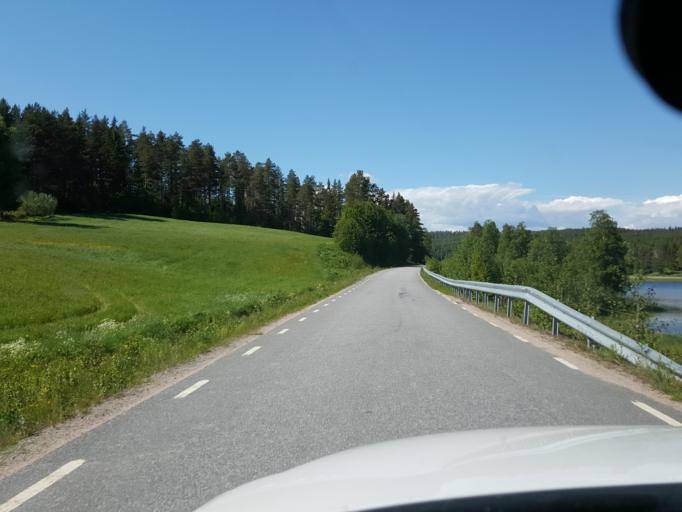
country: SE
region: Gaevleborg
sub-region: Ljusdals Kommun
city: Jaervsoe
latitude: 61.7397
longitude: 16.2764
